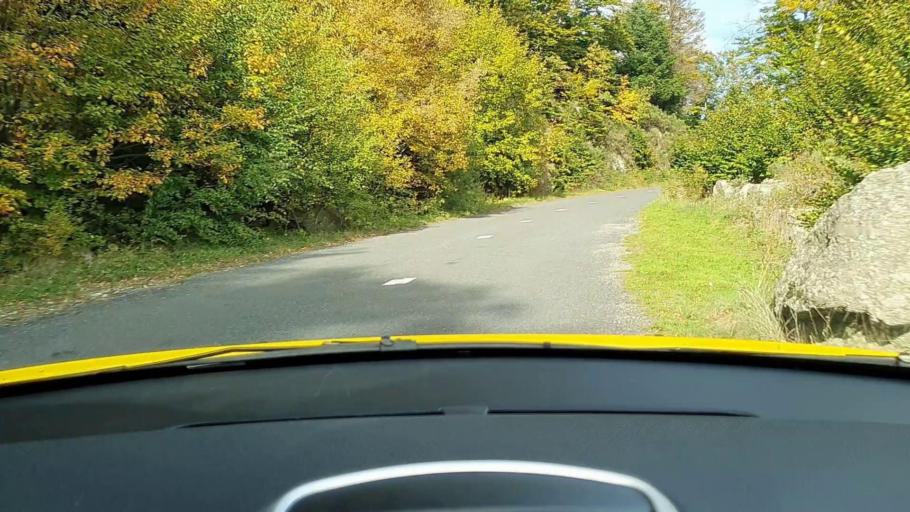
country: FR
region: Languedoc-Roussillon
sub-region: Departement du Gard
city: Valleraugue
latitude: 44.0533
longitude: 3.5799
